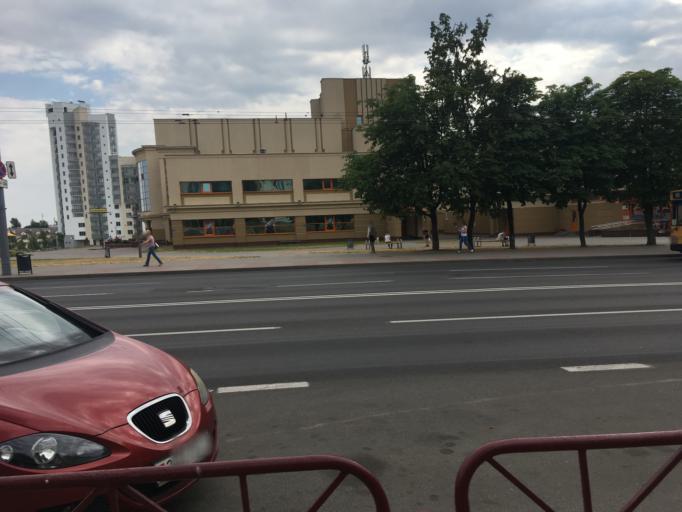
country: BY
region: Grodnenskaya
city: Hrodna
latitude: 53.6755
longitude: 23.8523
